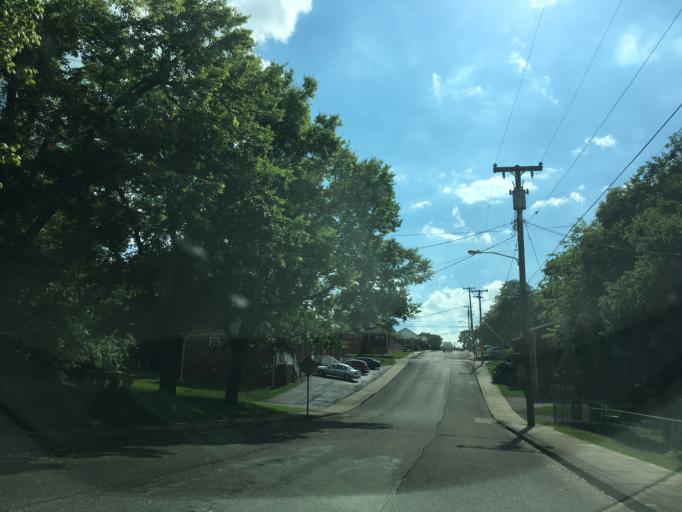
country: US
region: Tennessee
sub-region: Davidson County
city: Nashville
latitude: 36.1607
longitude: -86.8230
